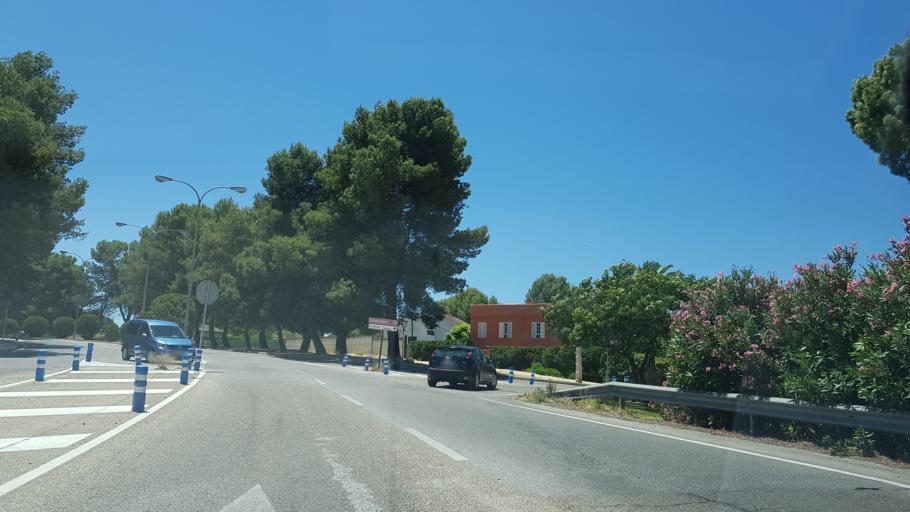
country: ES
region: Andalusia
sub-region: Provincia de Sevilla
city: Dos Hermanas
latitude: 37.3345
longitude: -5.9201
